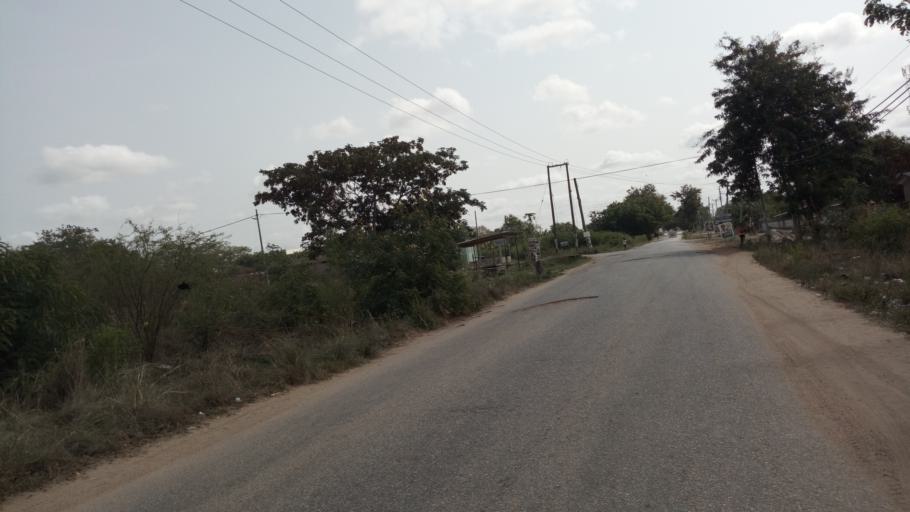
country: GH
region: Central
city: Winneba
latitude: 5.3689
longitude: -0.6452
